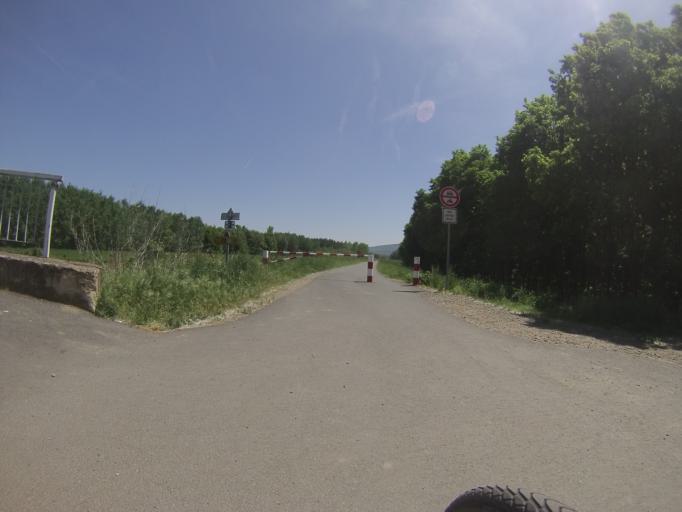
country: CZ
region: South Moravian
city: Vranovice
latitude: 48.9173
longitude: 16.5988
